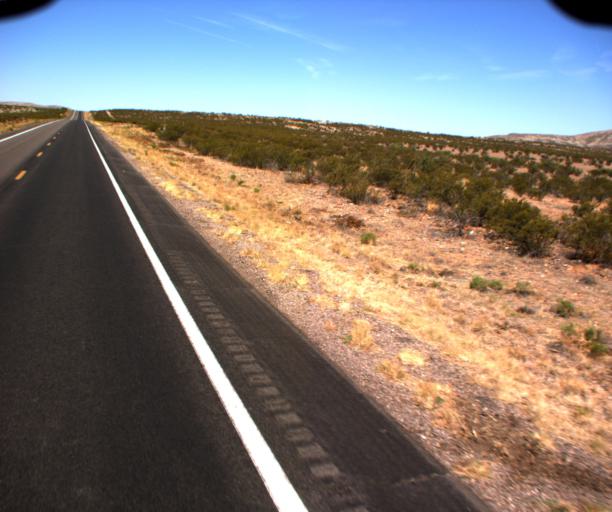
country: US
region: Arizona
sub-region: Greenlee County
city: Clifton
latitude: 32.7323
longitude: -109.1528
